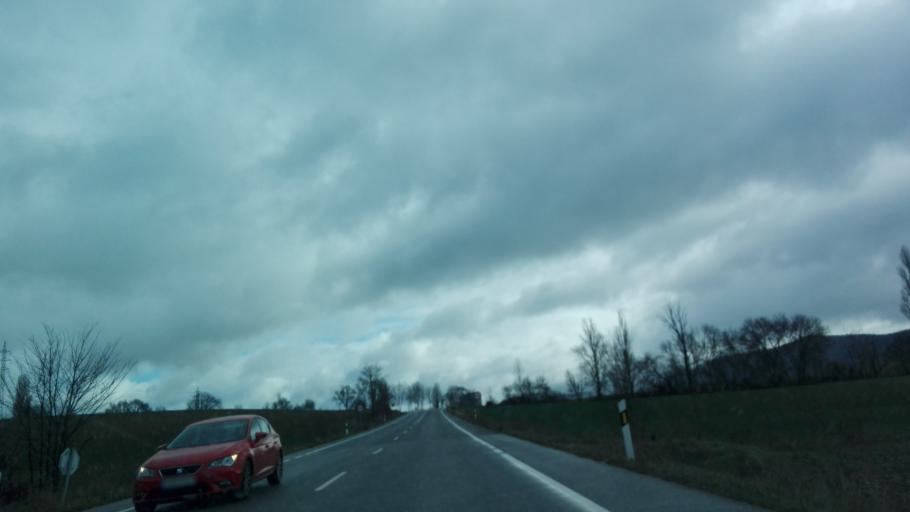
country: ES
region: Navarre
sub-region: Provincia de Navarra
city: Lizoain
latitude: 42.8143
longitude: -1.5073
